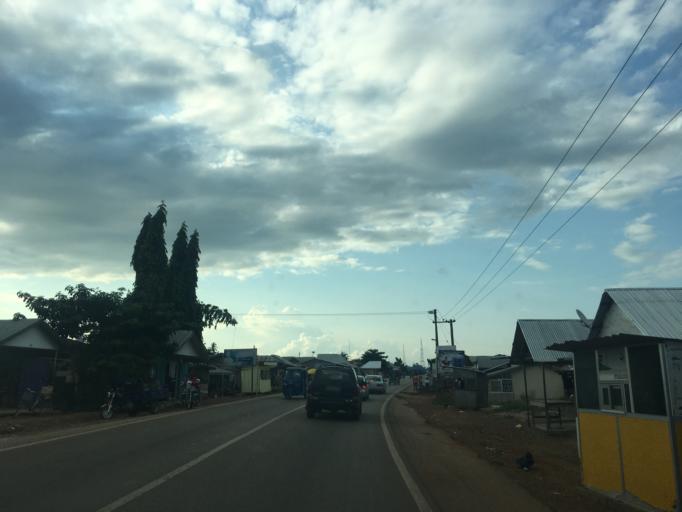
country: GH
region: Western
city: Bibiani
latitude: 6.4437
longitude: -2.3139
